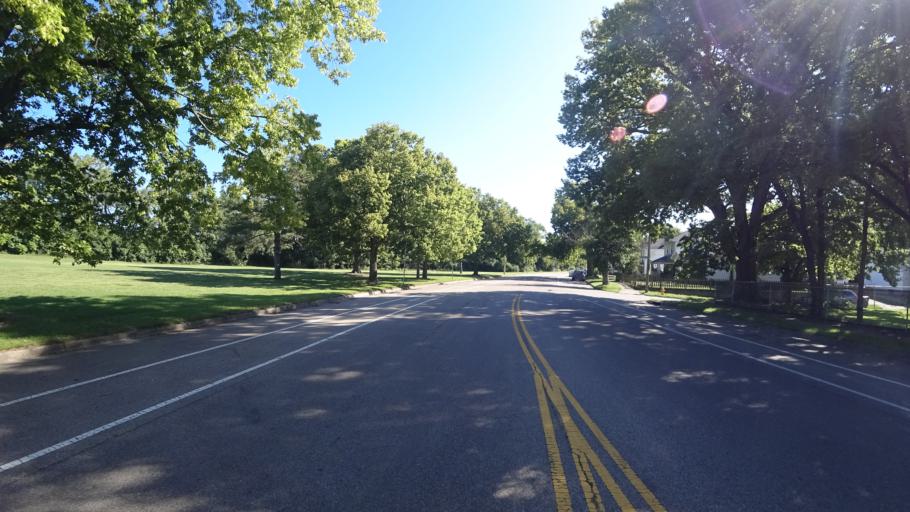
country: US
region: Ohio
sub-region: Butler County
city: Hamilton
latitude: 39.4072
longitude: -84.5468
